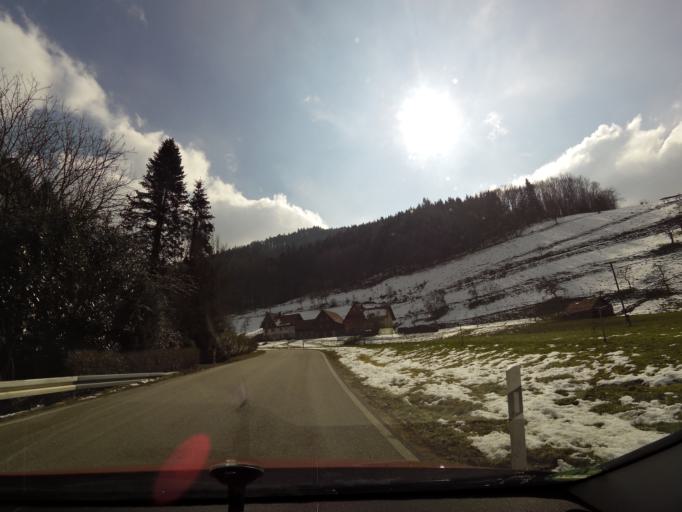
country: DE
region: Baden-Wuerttemberg
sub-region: Freiburg Region
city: Ottenhofen im Schwarzwald
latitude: 48.5480
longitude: 8.1673
